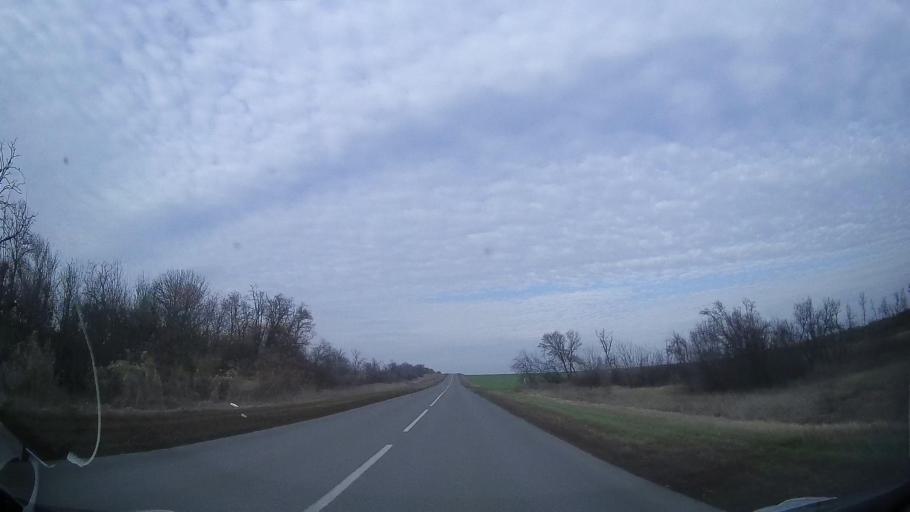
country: RU
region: Rostov
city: Zernograd
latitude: 46.9028
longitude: 40.3389
